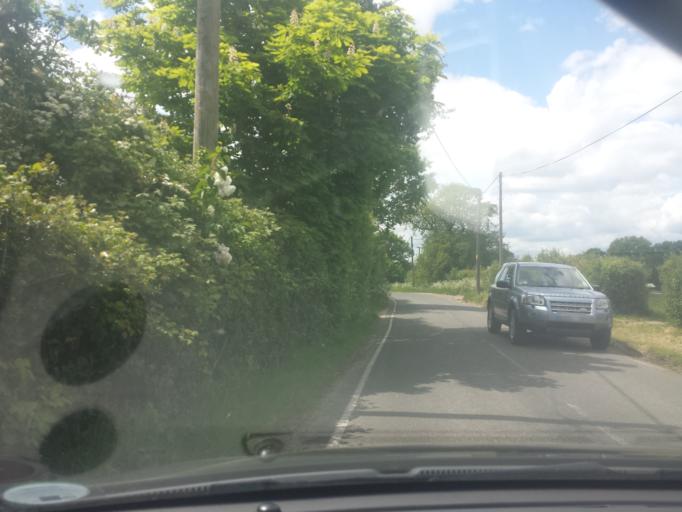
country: GB
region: England
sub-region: Essex
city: Little Clacton
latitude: 51.8815
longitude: 1.1612
